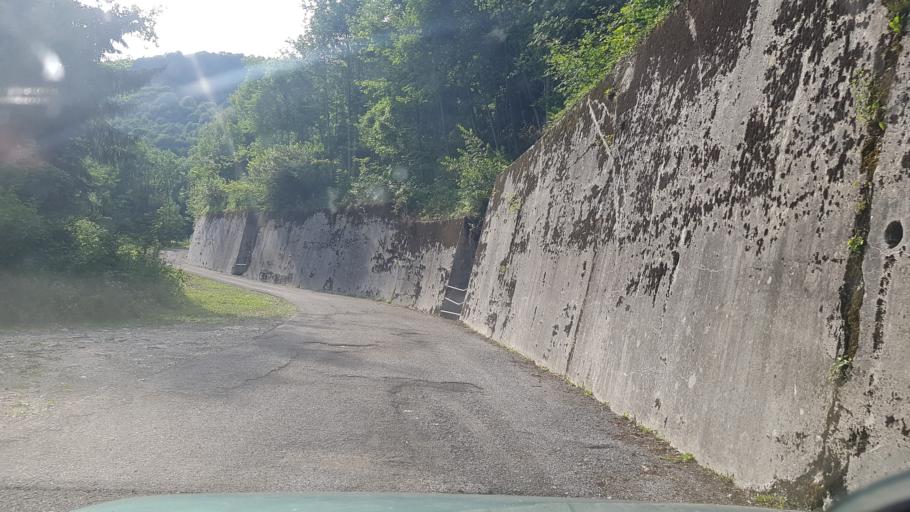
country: IT
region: Friuli Venezia Giulia
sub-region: Provincia di Udine
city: Torreano
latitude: 46.1780
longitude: 13.4256
